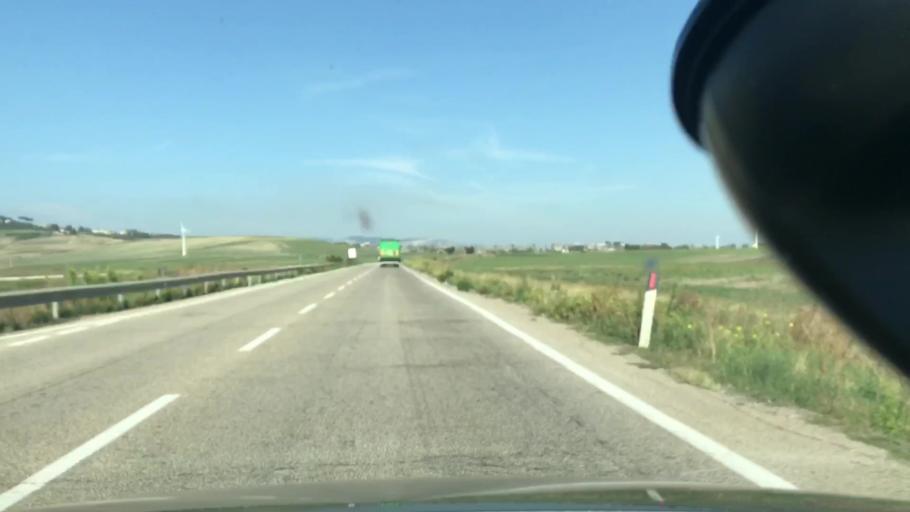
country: IT
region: Apulia
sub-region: Provincia di Foggia
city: Candela
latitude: 41.1336
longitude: 15.5493
